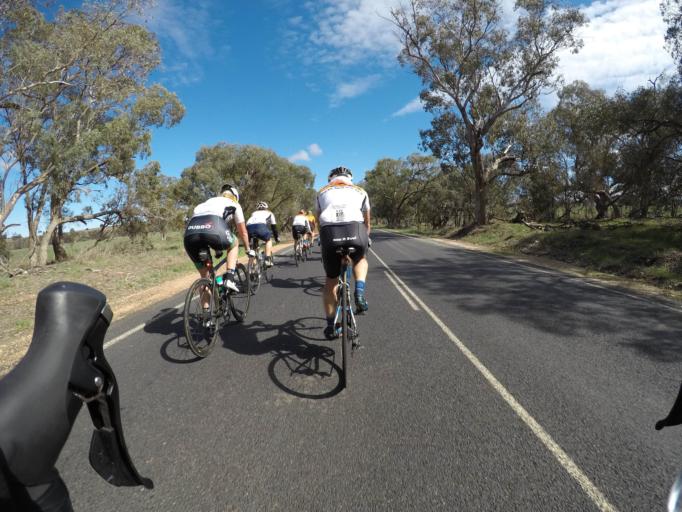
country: AU
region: New South Wales
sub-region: Parkes
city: Peak Hill
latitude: -32.7348
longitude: 148.5737
